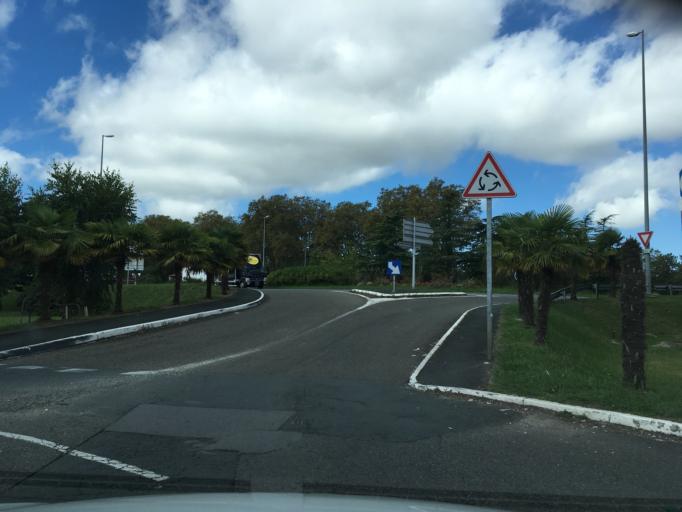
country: FR
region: Aquitaine
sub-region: Departement des Pyrenees-Atlantiques
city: Boucau
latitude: 43.5045
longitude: -1.4456
